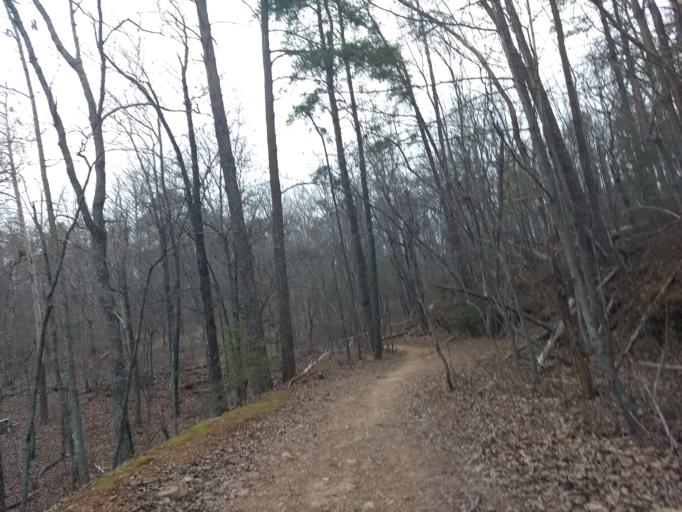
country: US
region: South Carolina
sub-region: Greenville County
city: Travelers Rest
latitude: 34.9421
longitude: -82.3976
